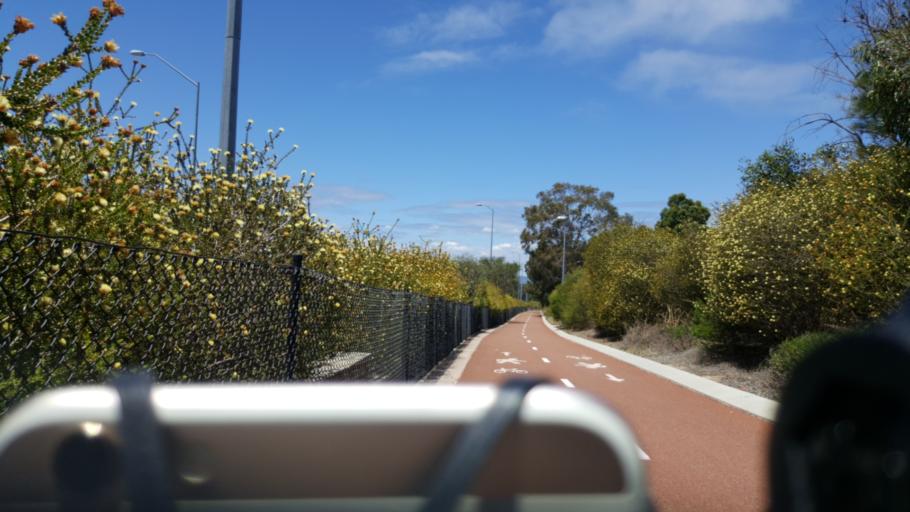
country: AU
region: Western Australia
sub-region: Stirling
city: Westminster
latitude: -31.8673
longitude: 115.8722
